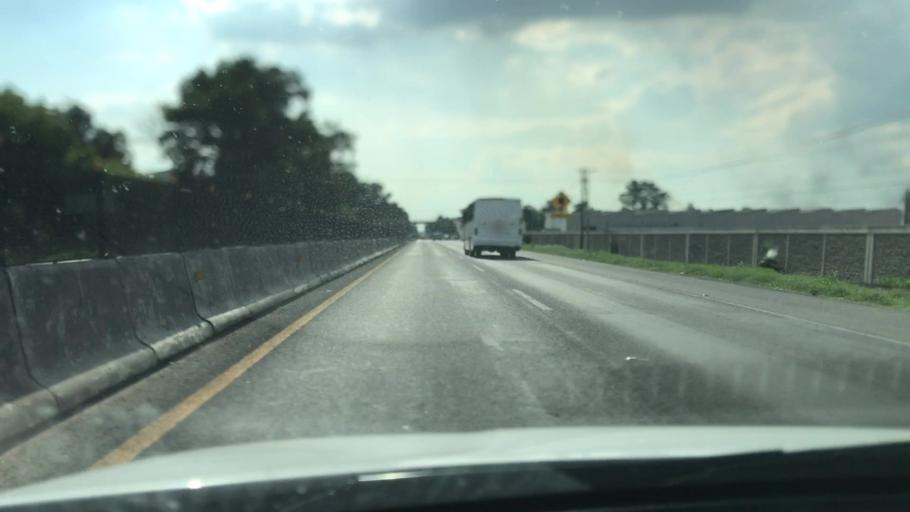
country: MX
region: Guanajuato
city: Valtierrilla
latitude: 20.5513
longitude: -101.1457
